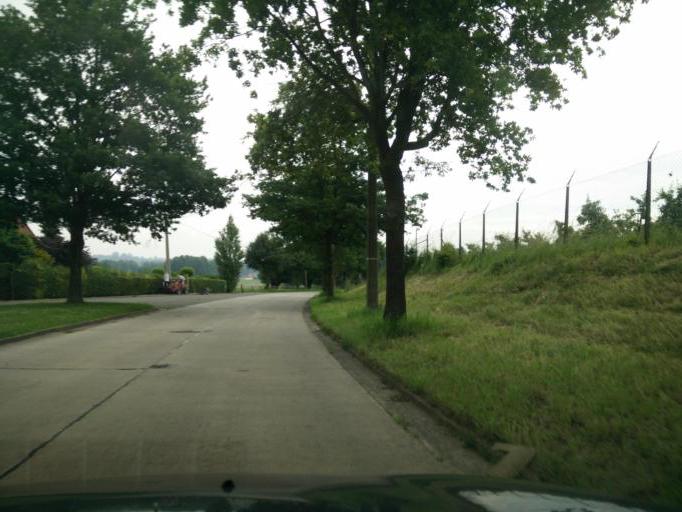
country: BE
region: Wallonia
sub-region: Province du Hainaut
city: Flobecq
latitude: 50.7855
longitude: 3.7414
